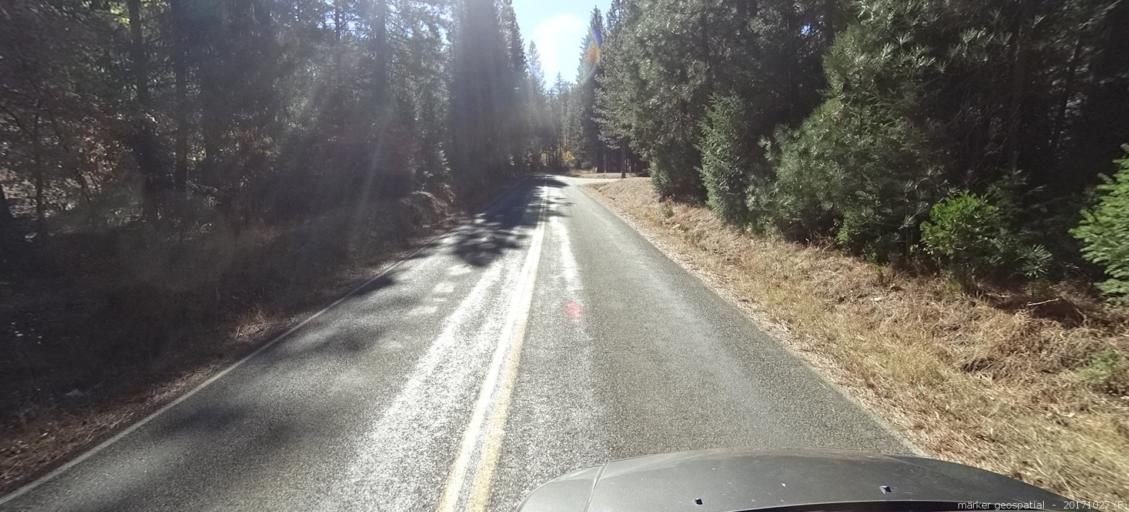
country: US
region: California
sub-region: Shasta County
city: Shingletown
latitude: 40.6997
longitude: -121.9220
